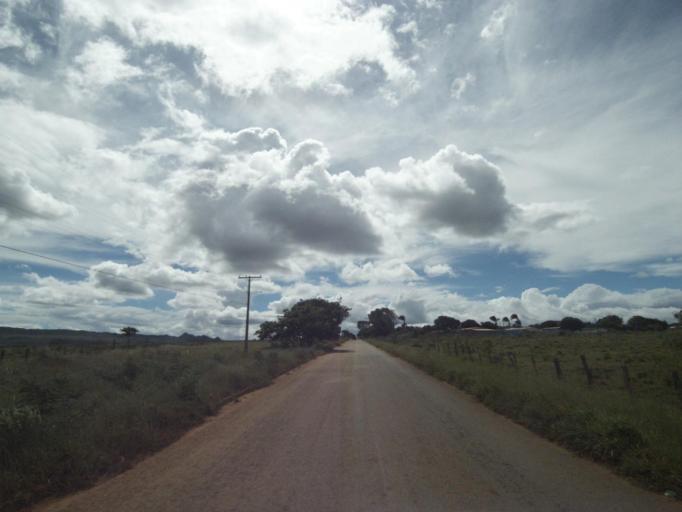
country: BR
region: Goias
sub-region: Pirenopolis
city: Pirenopolis
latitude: -15.7866
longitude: -48.7830
